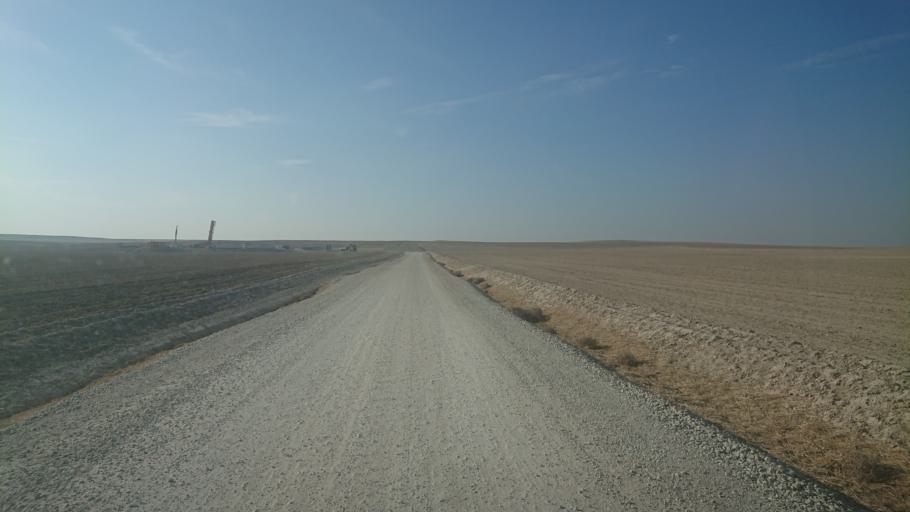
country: TR
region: Aksaray
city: Sultanhani
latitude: 38.0707
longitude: 33.6132
